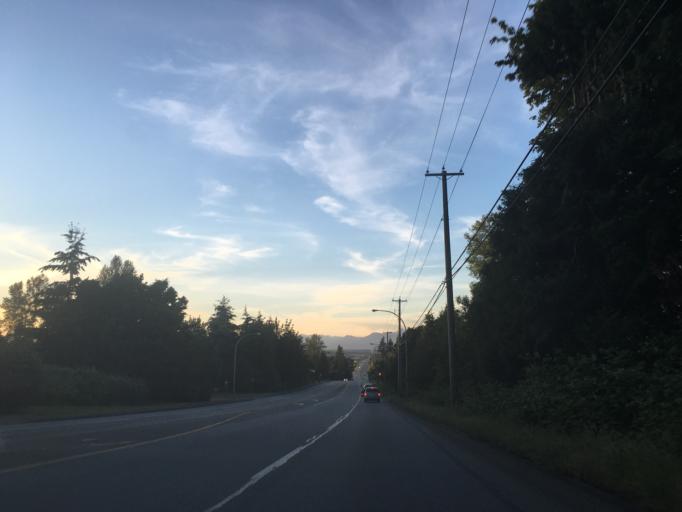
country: US
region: Washington
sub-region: Whatcom County
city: Blaine
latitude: 49.0529
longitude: -122.7352
